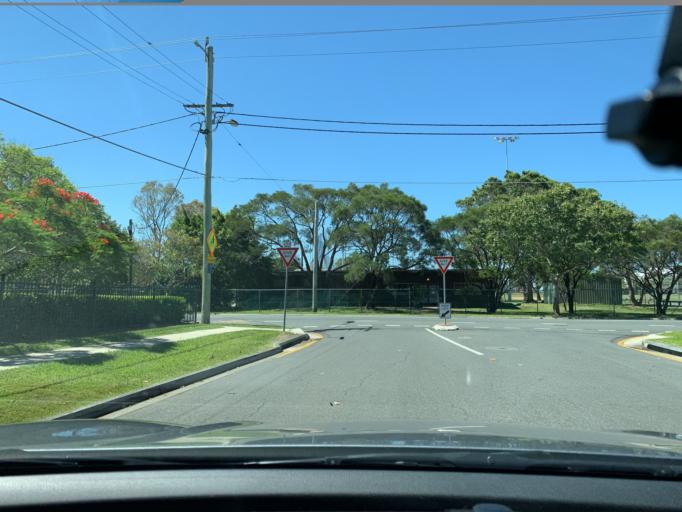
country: AU
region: Queensland
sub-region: Brisbane
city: Ascot
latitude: -27.4190
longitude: 153.0696
